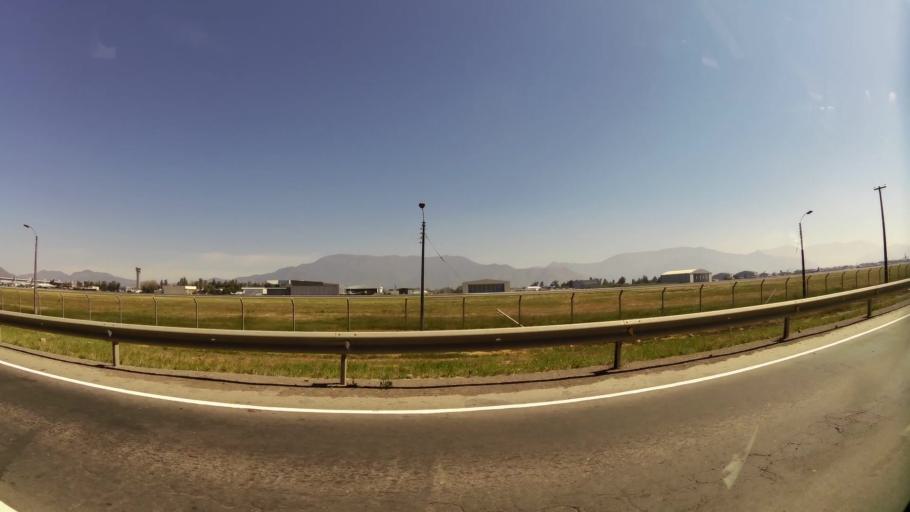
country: CL
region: Santiago Metropolitan
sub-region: Provincia de Santiago
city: Lo Prado
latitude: -33.3853
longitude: -70.7838
